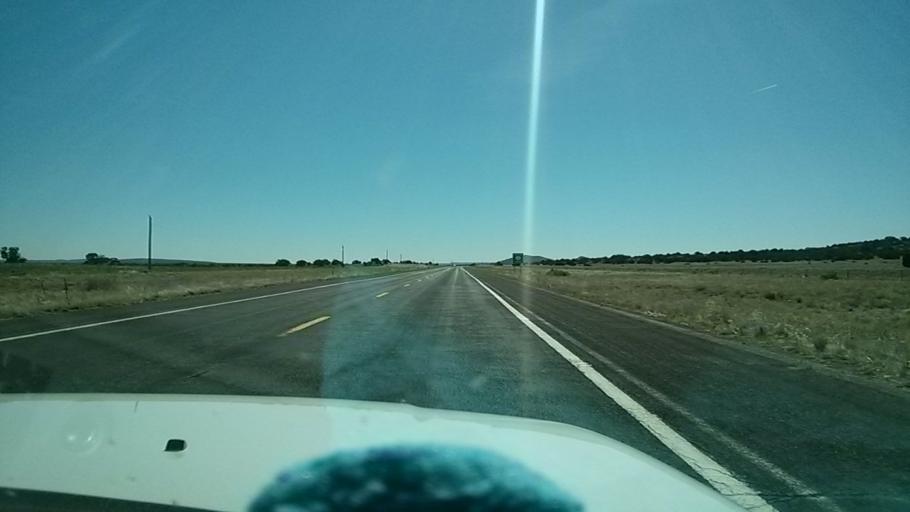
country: US
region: Arizona
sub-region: Mohave County
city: Peach Springs
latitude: 35.5537
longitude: -113.3309
